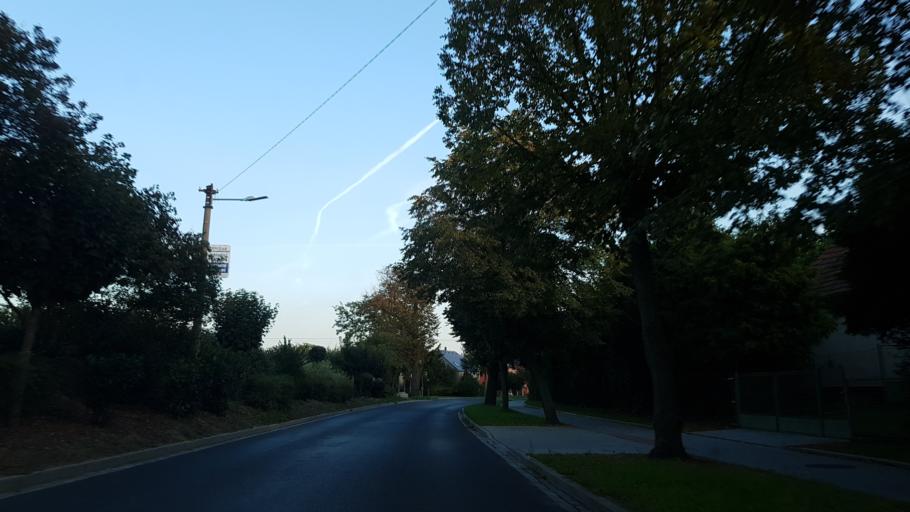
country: CZ
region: Zlin
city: Polesovice
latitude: 49.0289
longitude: 17.3509
